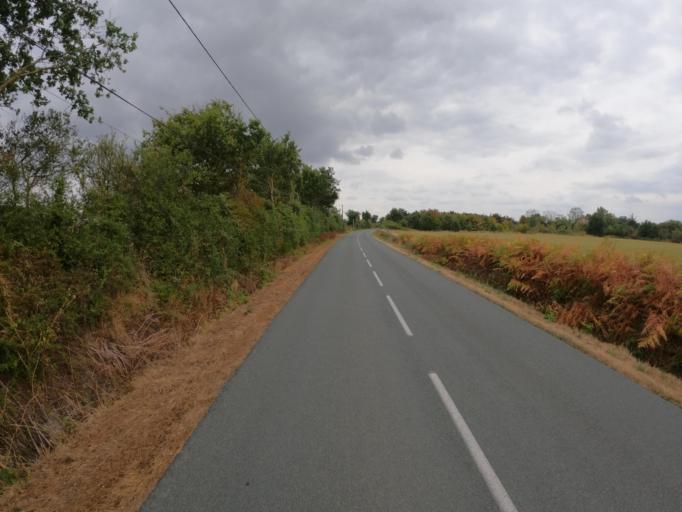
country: FR
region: Pays de la Loire
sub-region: Departement de la Vendee
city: Tiffauges
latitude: 47.0030
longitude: -1.0967
